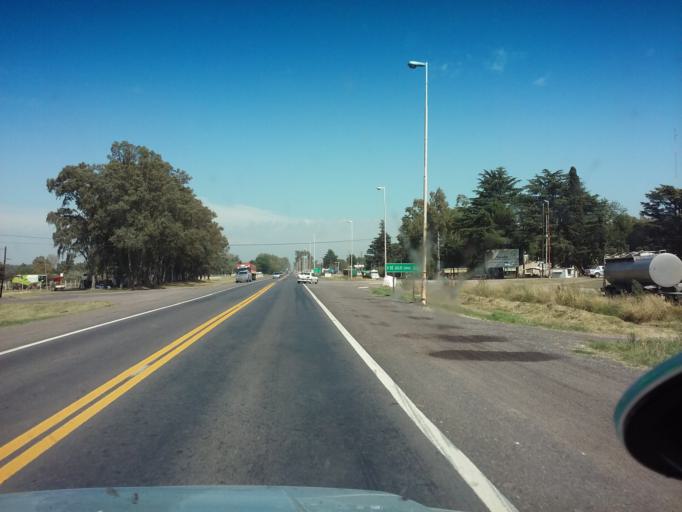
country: AR
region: Buenos Aires
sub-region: Partido de Nueve de Julio
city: Nueve de Julio
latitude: -35.4738
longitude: -60.8606
